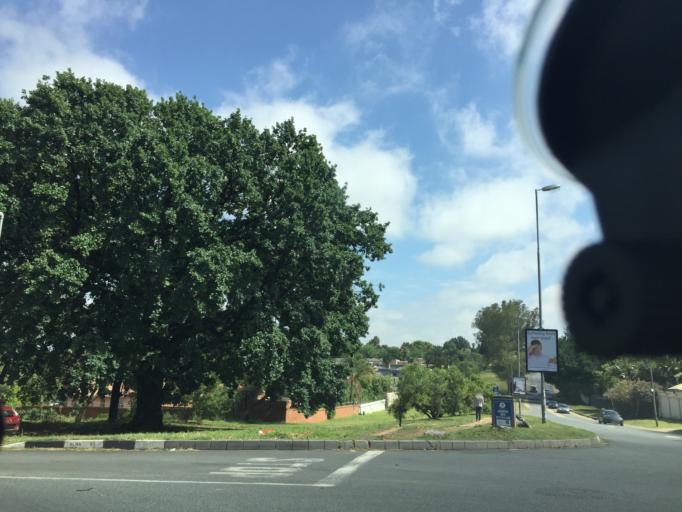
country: ZA
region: Gauteng
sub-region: City of Johannesburg Metropolitan Municipality
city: Modderfontein
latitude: -26.0805
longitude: 28.0796
